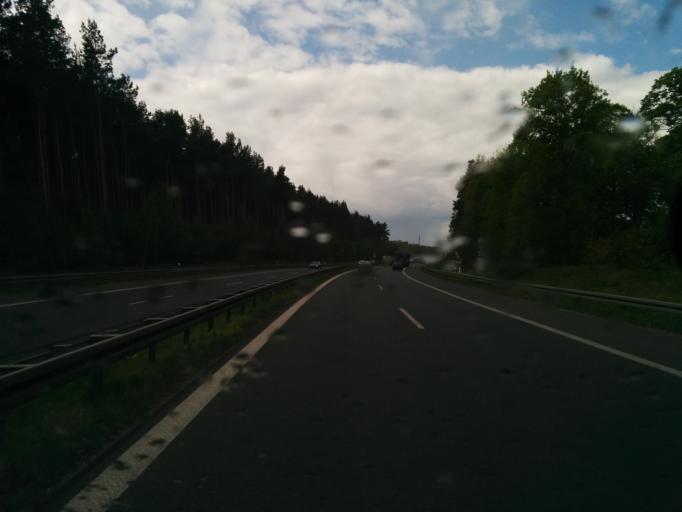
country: DE
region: Brandenburg
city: Dallgow-Doeberitz
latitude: 52.5346
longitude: 13.0699
